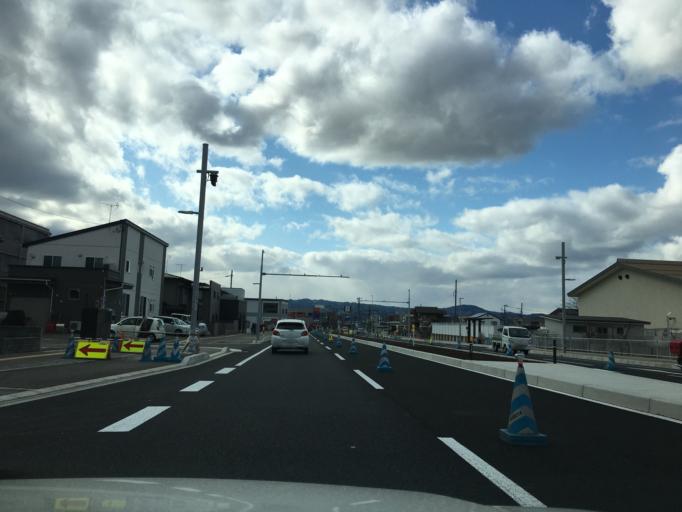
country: JP
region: Yamagata
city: Yamagata-shi
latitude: 38.2597
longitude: 140.3278
